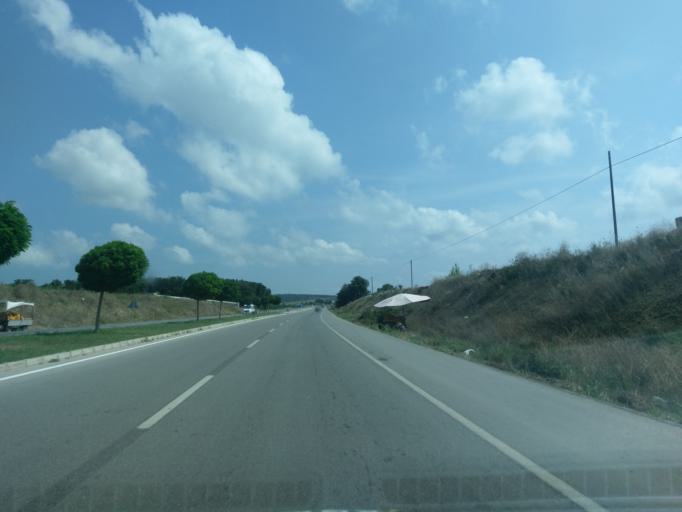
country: TR
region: Samsun
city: Bafra
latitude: 41.6031
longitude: 35.8212
